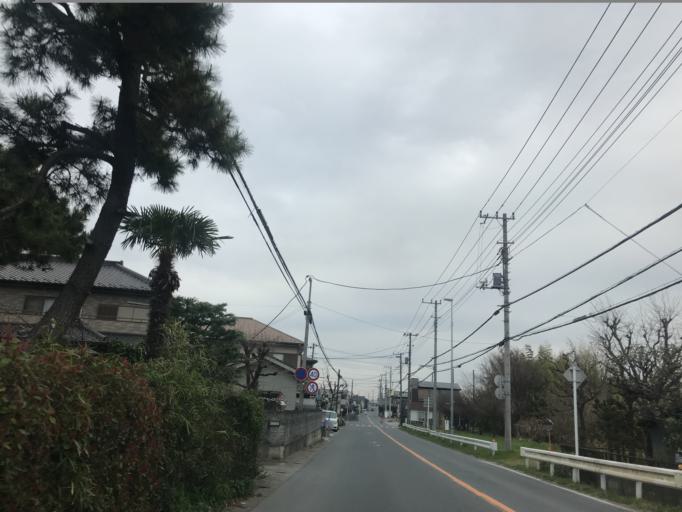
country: JP
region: Saitama
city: Yashio-shi
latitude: 35.8362
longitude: 139.8410
